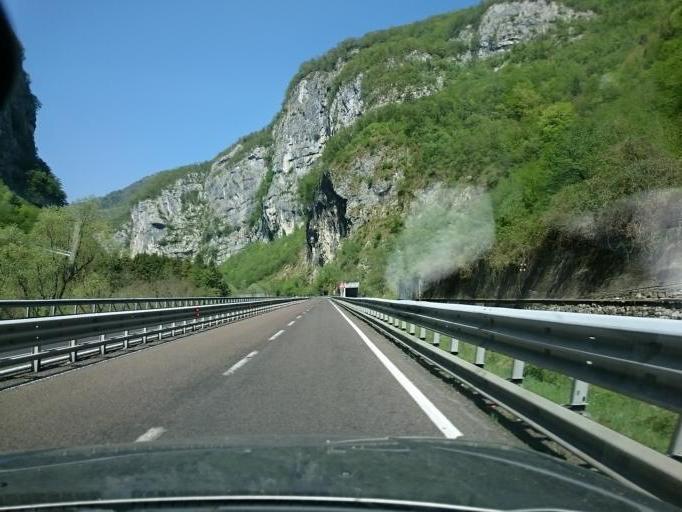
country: IT
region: Veneto
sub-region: Provincia di Vicenza
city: Enego
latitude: 45.9420
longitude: 11.7260
